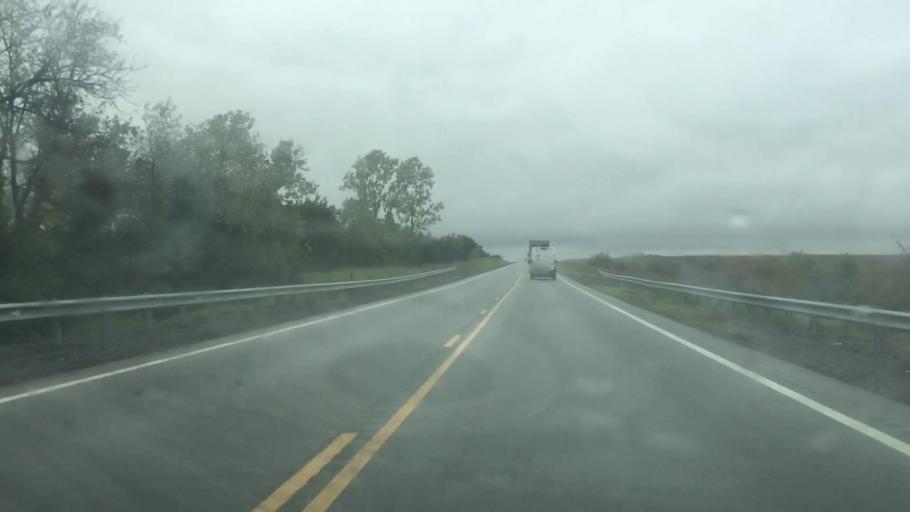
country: US
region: Kansas
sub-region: Anderson County
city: Garnett
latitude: 38.1505
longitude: -95.3188
